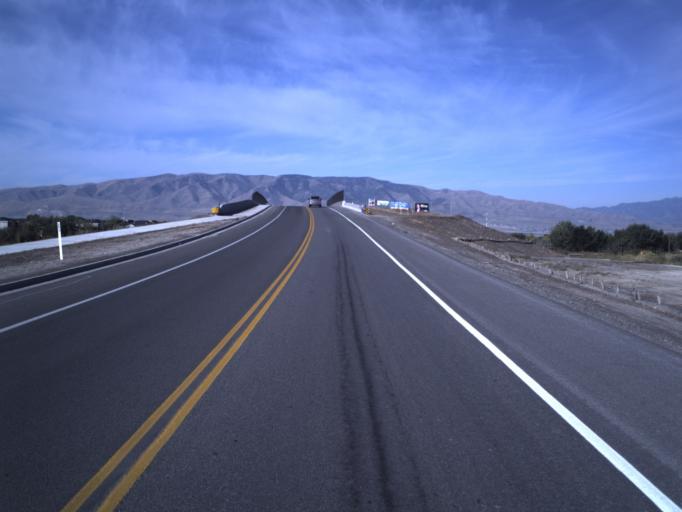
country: US
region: Utah
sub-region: Utah County
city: Lindon
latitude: 40.3113
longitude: -111.7461
